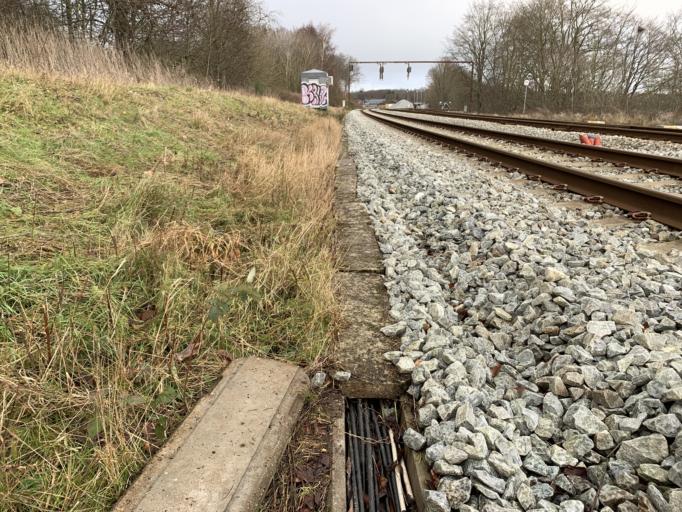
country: DK
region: North Denmark
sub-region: Mariagerfjord Kommune
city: Hobro
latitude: 56.6387
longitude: 9.7777
